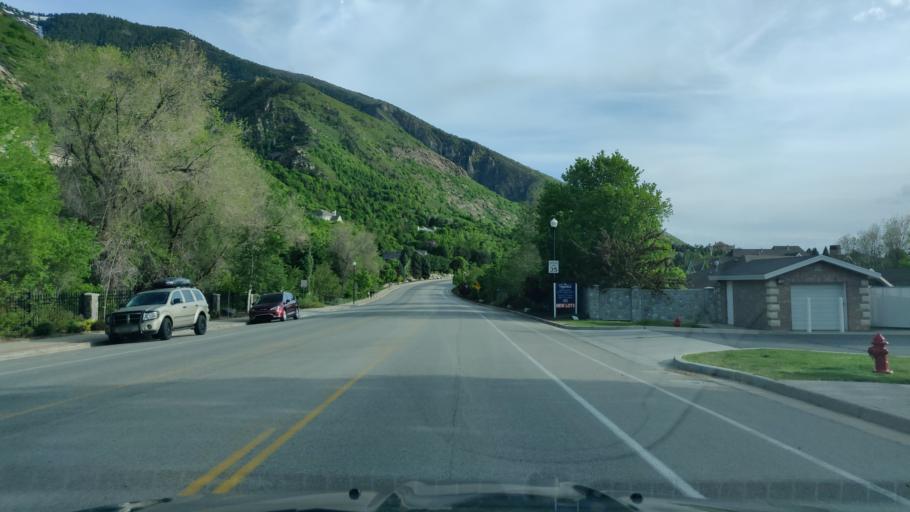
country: US
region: Utah
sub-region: Salt Lake County
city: Granite
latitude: 40.5478
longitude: -111.8065
